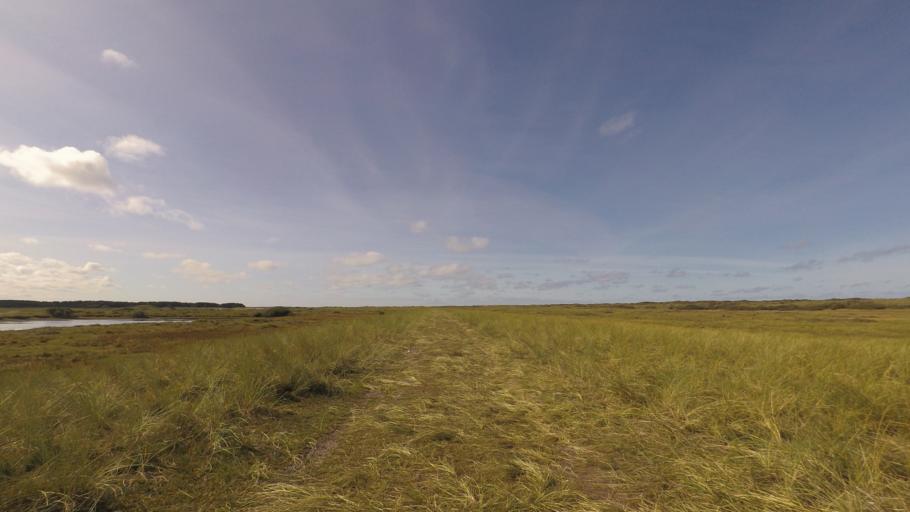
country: NL
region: Friesland
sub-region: Gemeente Ameland
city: Nes
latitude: 53.4535
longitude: 5.7122
